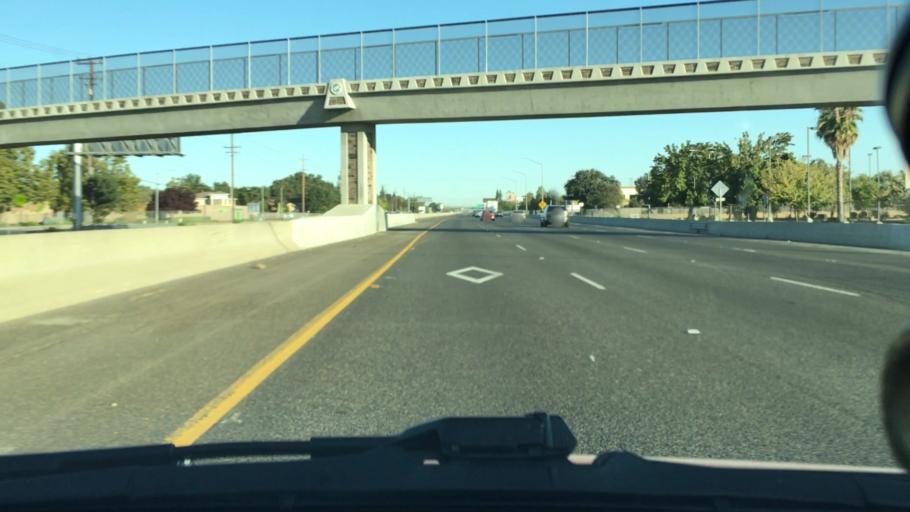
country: US
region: California
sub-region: Sacramento County
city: Elk Grove
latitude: 38.4123
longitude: -121.3901
